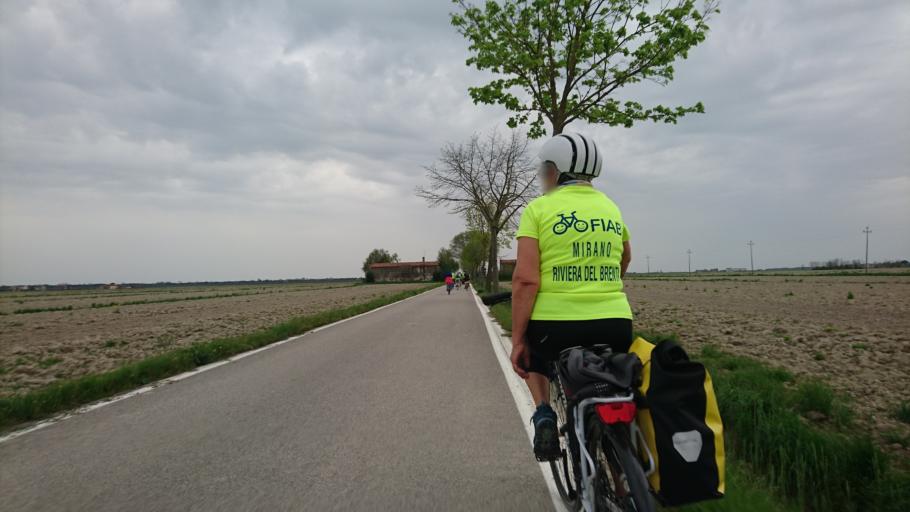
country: IT
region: Veneto
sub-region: Provincia di Venezia
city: Bibione
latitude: 45.6572
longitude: 13.0015
